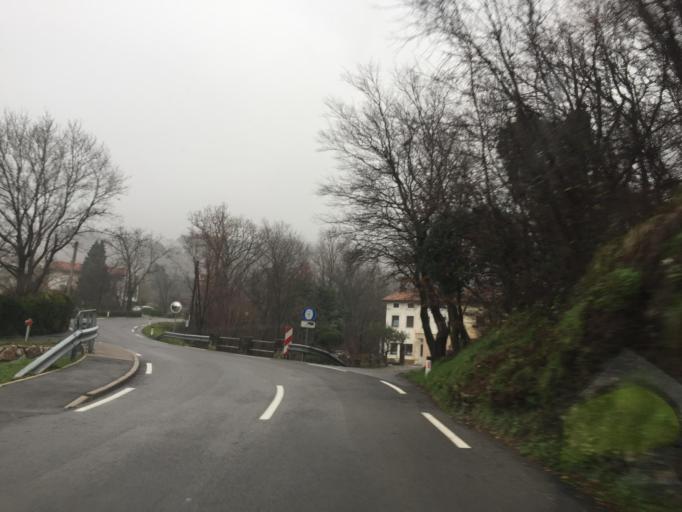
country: SI
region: Ajdovscina
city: Lokavec
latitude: 45.9116
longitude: 13.8919
